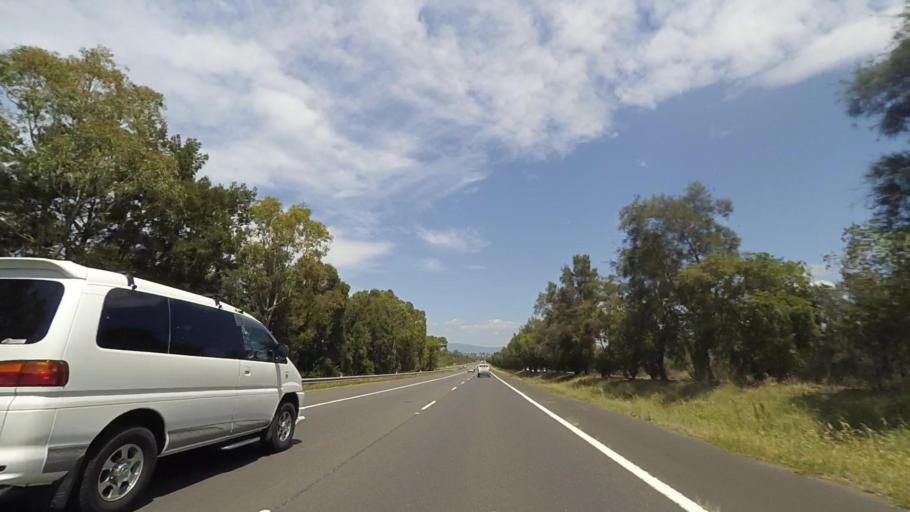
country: AU
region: New South Wales
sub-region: Wollongong
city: Berkeley
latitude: -34.4748
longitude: 150.8307
